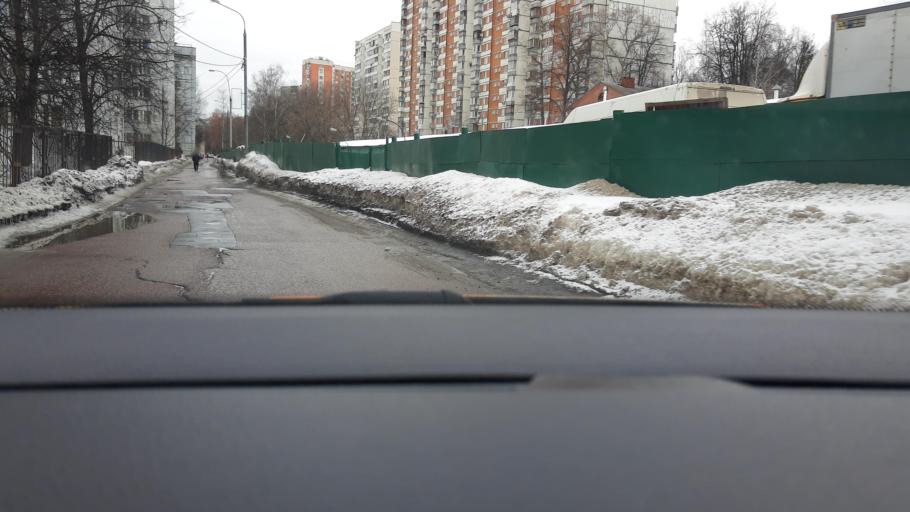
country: RU
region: Moscow
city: Babushkin
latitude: 55.8538
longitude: 37.7016
